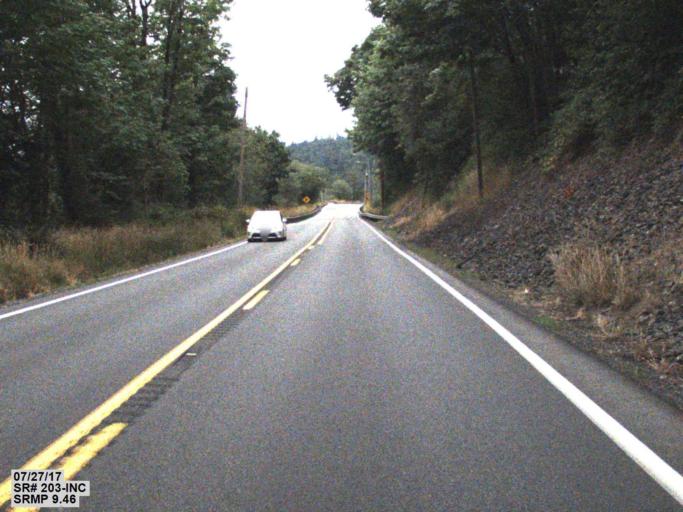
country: US
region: Washington
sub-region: King County
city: Lake Marcel-Stillwater
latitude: 47.6861
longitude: -121.9329
